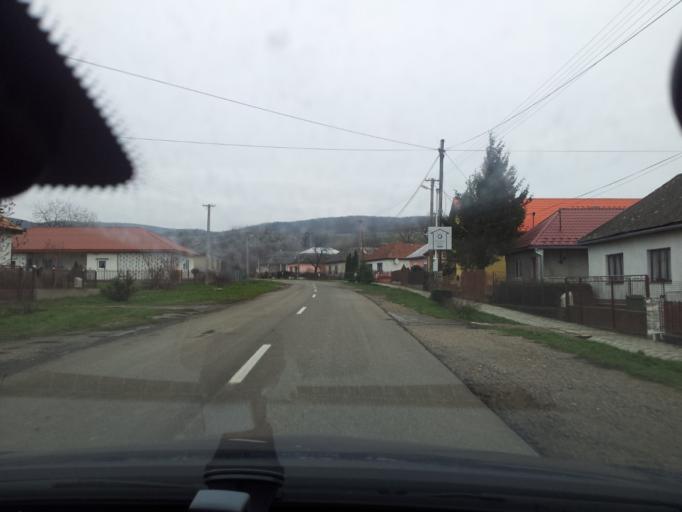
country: HU
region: Borsod-Abauj-Zemplen
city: Satoraljaujhely
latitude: 48.4527
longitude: 21.6777
